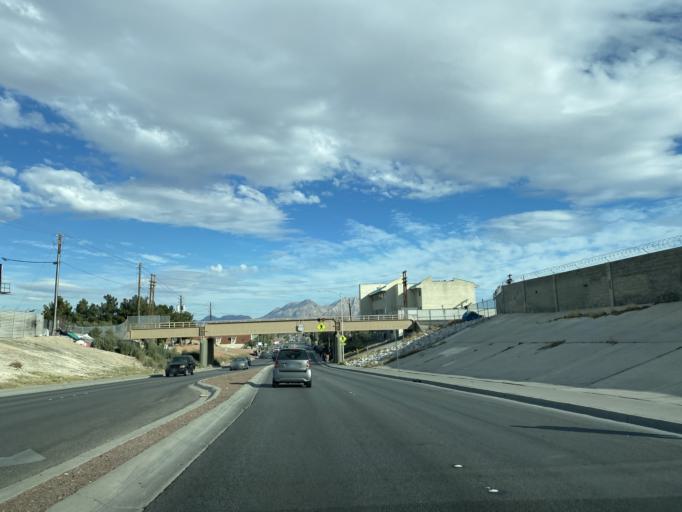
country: US
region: Nevada
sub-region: Clark County
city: Las Vegas
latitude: 36.1883
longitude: -115.1421
